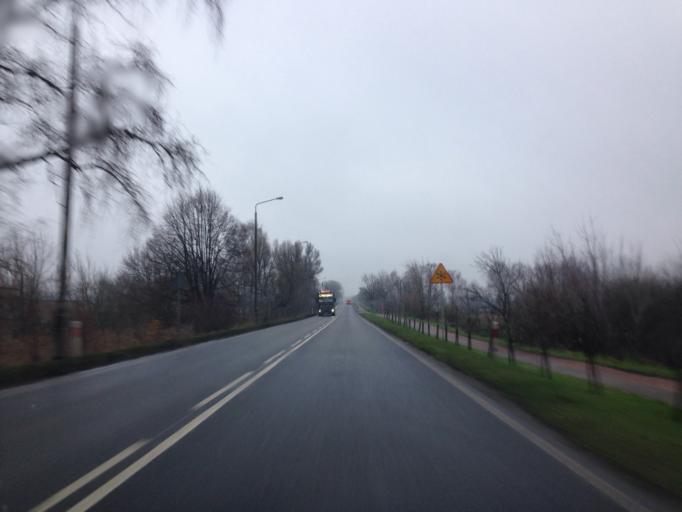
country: PL
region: Kujawsko-Pomorskie
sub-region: Powiat nakielski
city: Naklo nad Notecia
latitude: 53.1283
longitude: 17.6013
